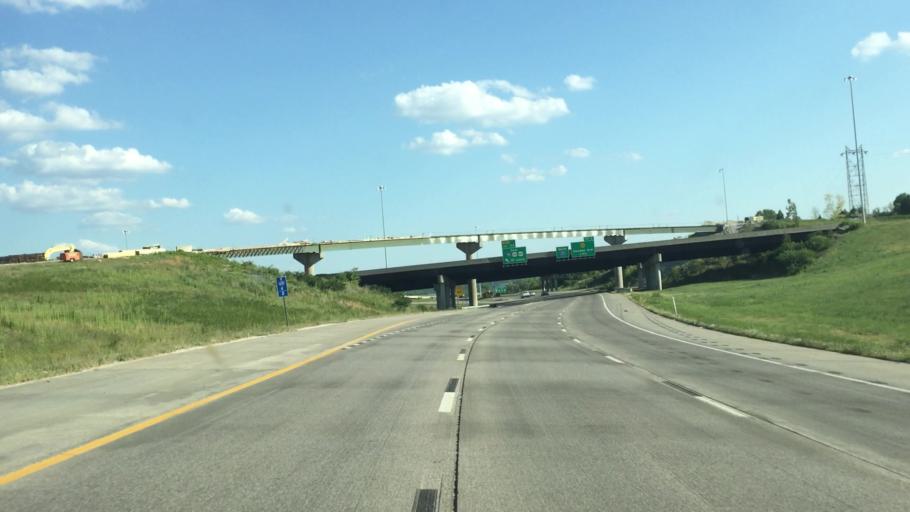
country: US
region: Kansas
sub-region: Wyandotte County
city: Kansas City
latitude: 39.1075
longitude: -94.6806
